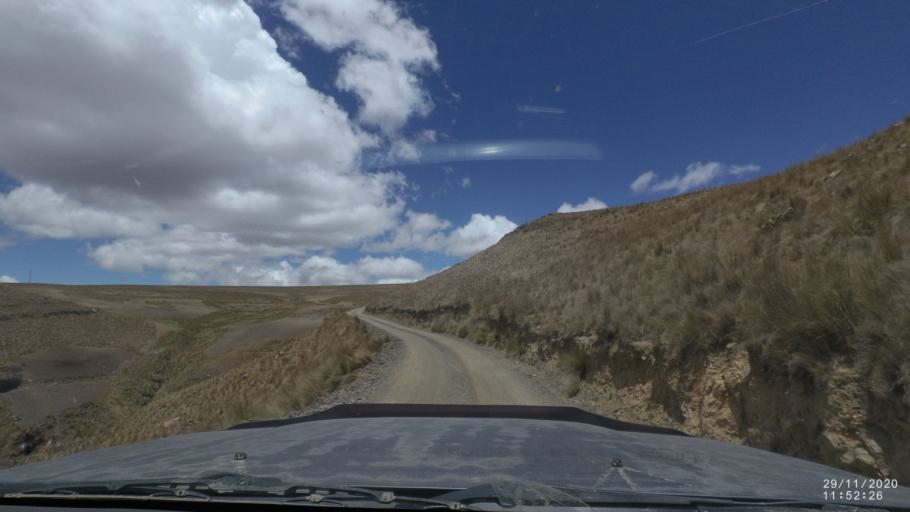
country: BO
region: Cochabamba
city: Cochabamba
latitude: -17.1698
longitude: -66.2662
